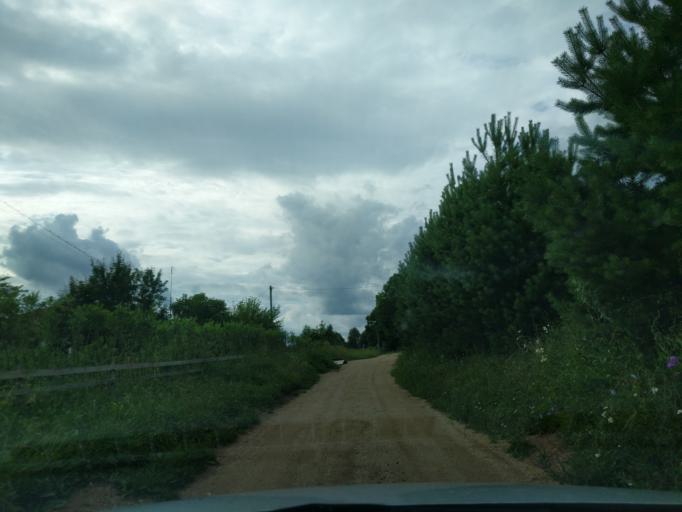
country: RU
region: Kaluga
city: Nikola-Lenivets
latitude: 54.7420
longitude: 35.6399
